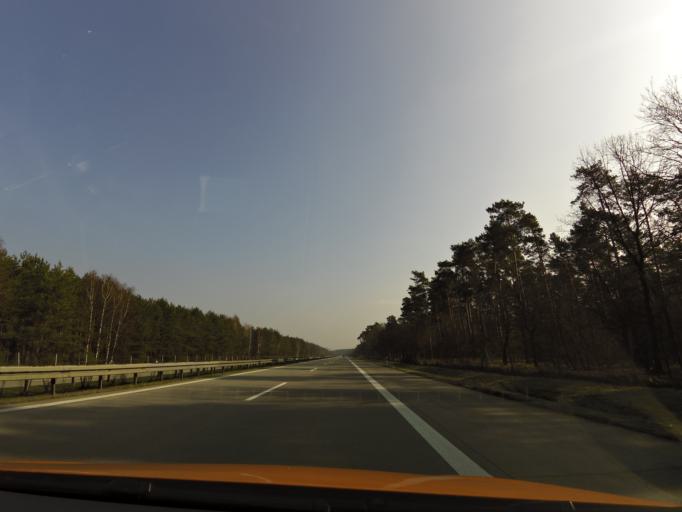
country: DE
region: Brandenburg
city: Berkenbruck
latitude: 52.3357
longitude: 14.1276
